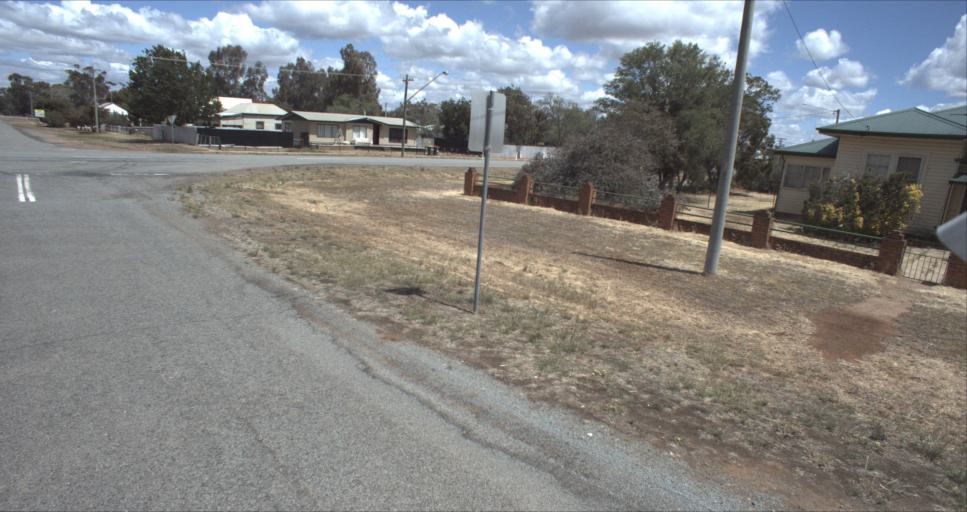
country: AU
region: New South Wales
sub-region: Murrumbidgee Shire
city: Darlington Point
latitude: -34.5171
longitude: 146.1806
